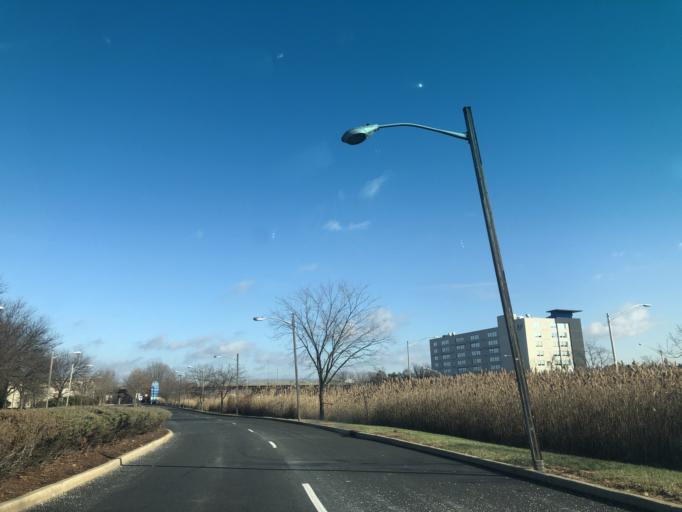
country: US
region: New Jersey
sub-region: Hudson County
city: Secaucus
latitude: 40.7900
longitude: -74.0484
